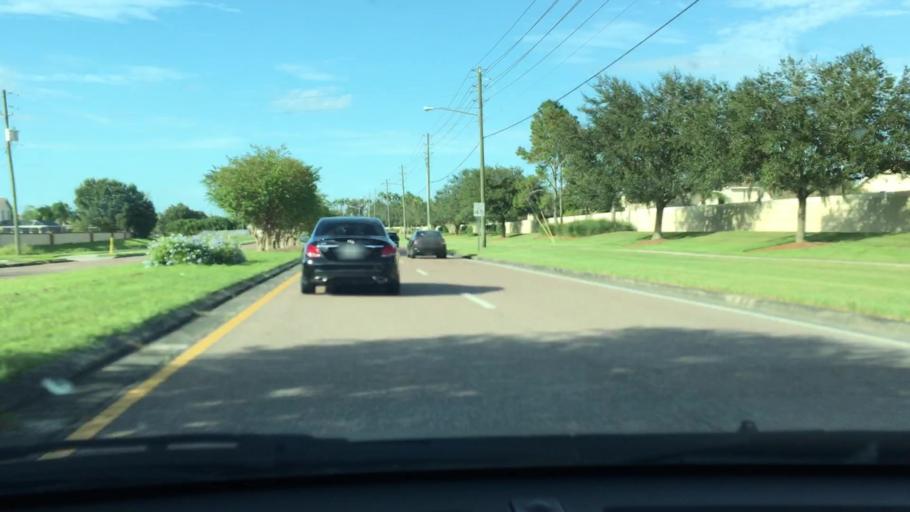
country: US
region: Florida
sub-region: Pasco County
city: Land O' Lakes
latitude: 28.2043
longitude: -82.4335
